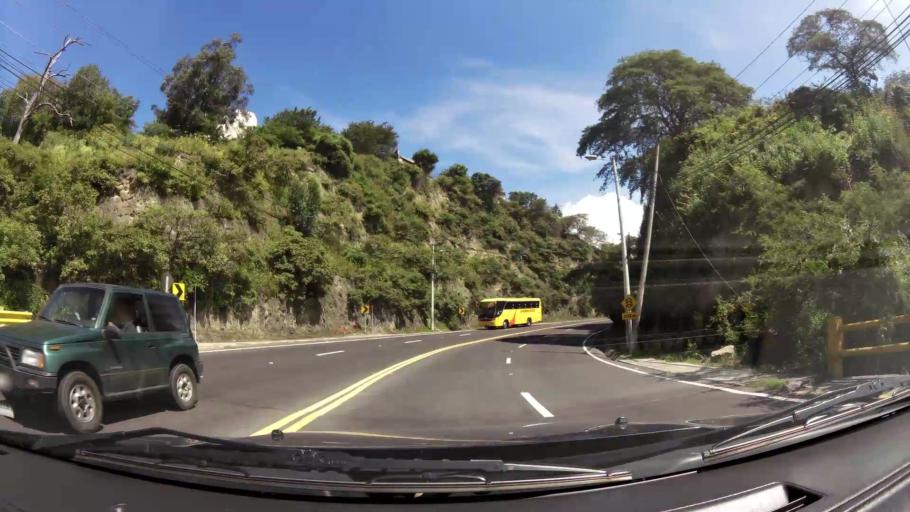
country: EC
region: Pichincha
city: Quito
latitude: -0.2115
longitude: -78.4238
